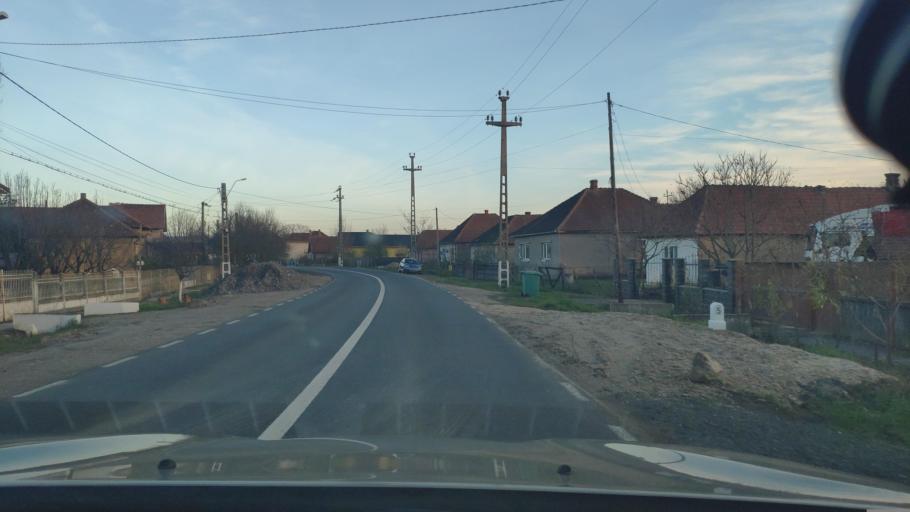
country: RO
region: Satu Mare
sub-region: Comuna Apa
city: Apa
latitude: 47.7641
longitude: 23.1885
